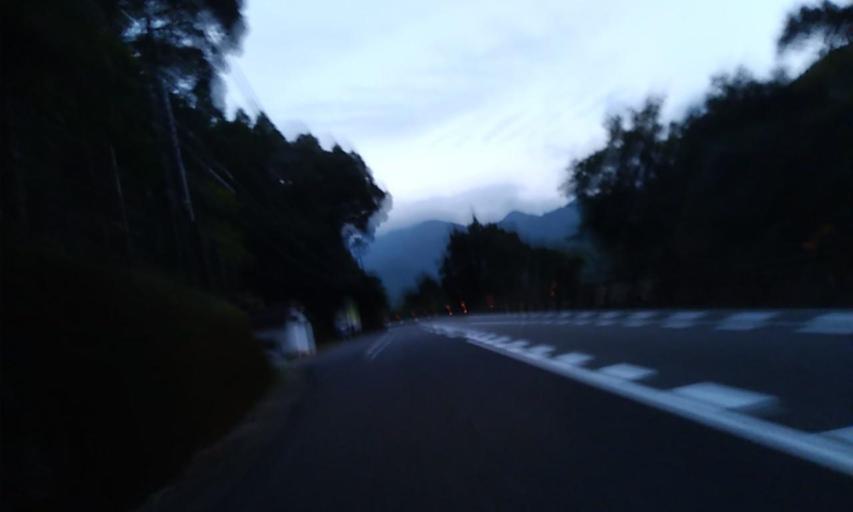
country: JP
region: Wakayama
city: Shingu
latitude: 33.7393
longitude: 135.9388
